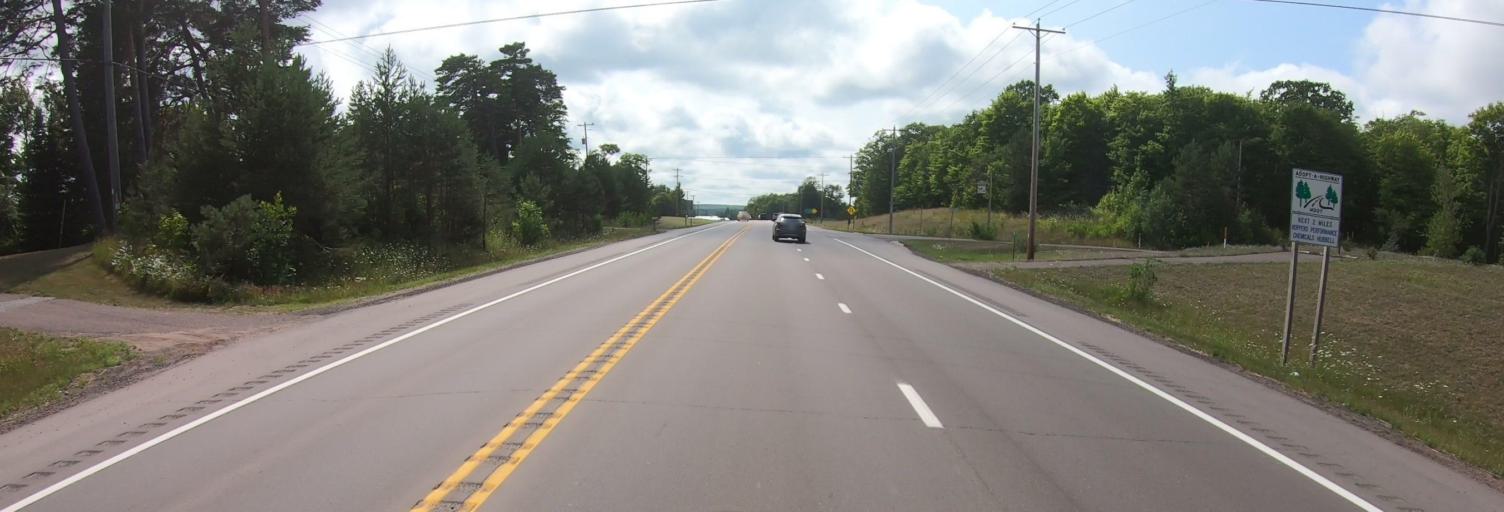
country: US
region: Michigan
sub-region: Houghton County
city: Hancock
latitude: 47.0998
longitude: -88.6107
